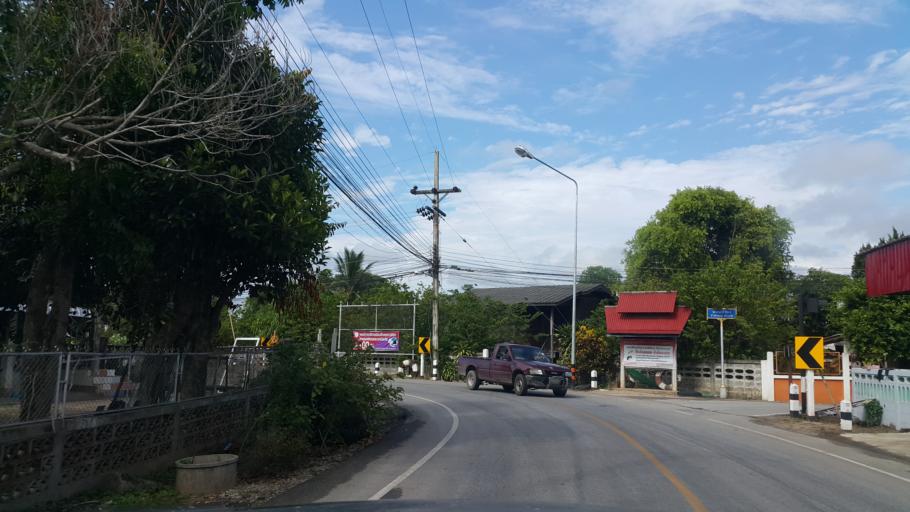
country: TH
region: Chiang Rai
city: Wiang Chai
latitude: 19.9187
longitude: 99.8921
